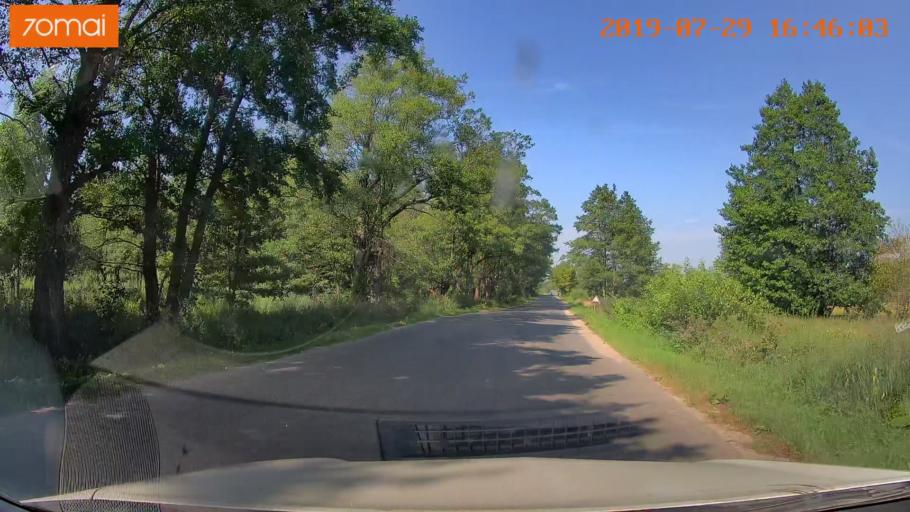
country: RU
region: Kaliningrad
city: Primorsk
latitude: 54.7706
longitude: 20.0805
